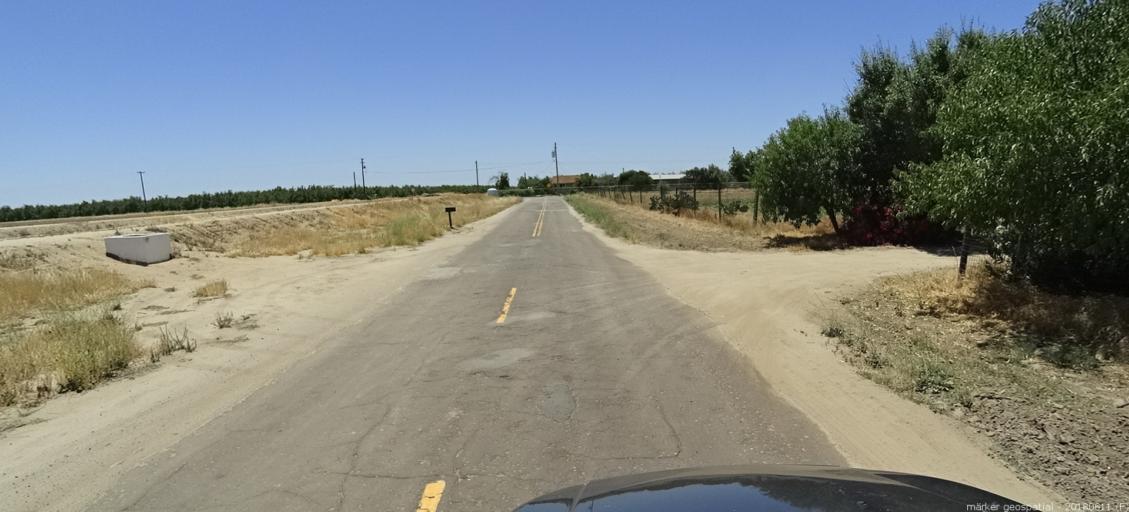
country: US
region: California
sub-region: Madera County
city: Fairmead
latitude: 37.0556
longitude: -120.1844
